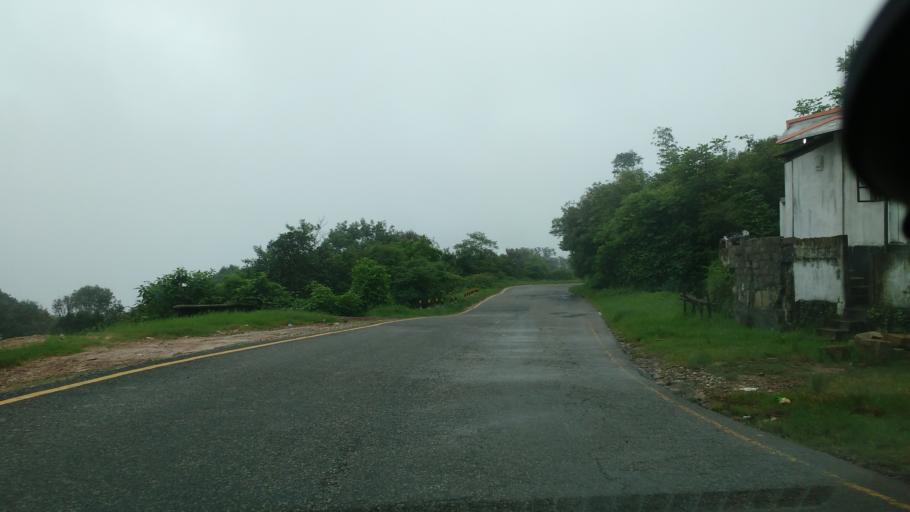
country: IN
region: Meghalaya
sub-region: East Khasi Hills
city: Cherrapunji
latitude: 25.2855
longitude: 91.7227
